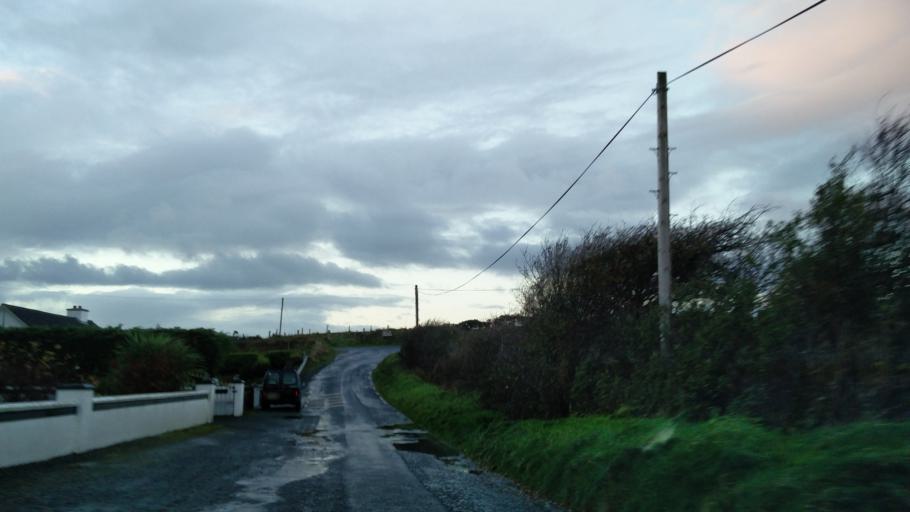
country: IE
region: Connaught
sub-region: Maigh Eo
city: Westport
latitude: 53.7817
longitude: -9.6684
